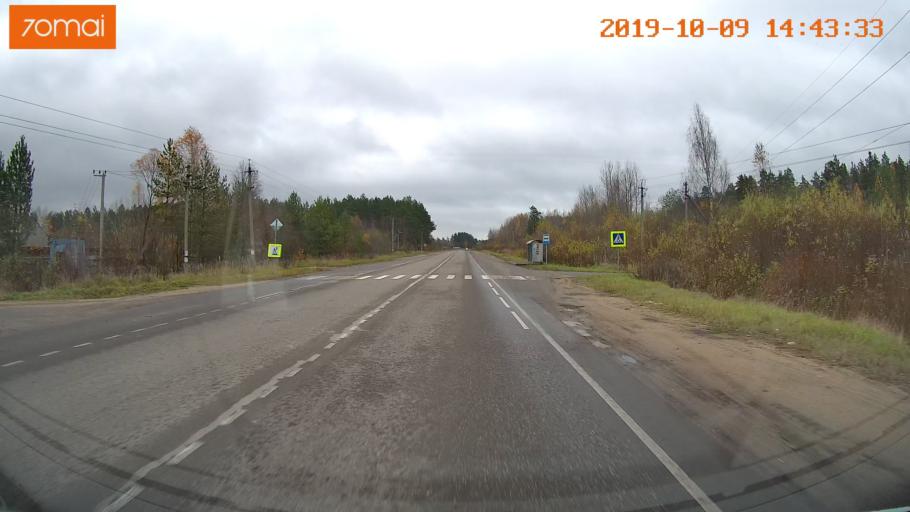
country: RU
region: Kostroma
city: Buy
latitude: 58.4575
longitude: 41.5460
